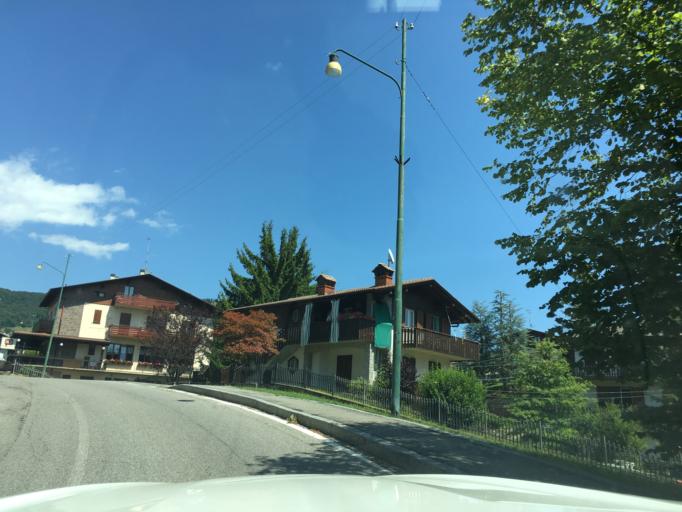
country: IT
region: Lombardy
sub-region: Provincia di Bergamo
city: Selvino
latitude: 45.7873
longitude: 9.7592
